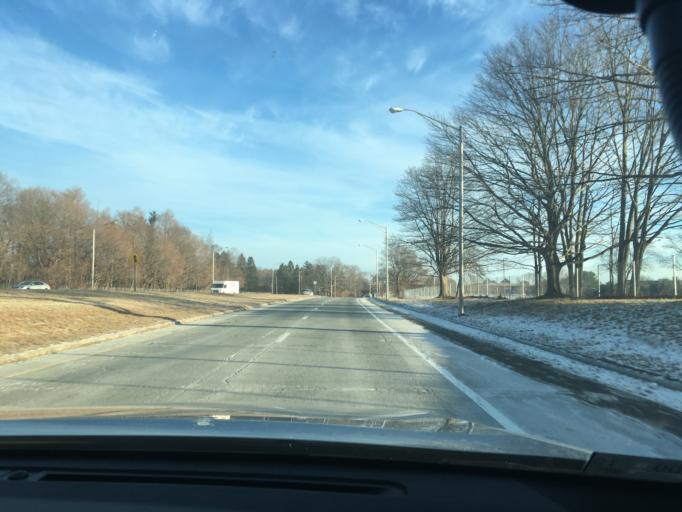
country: US
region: Rhode Island
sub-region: Providence County
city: Cranston
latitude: 41.7432
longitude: -71.4720
